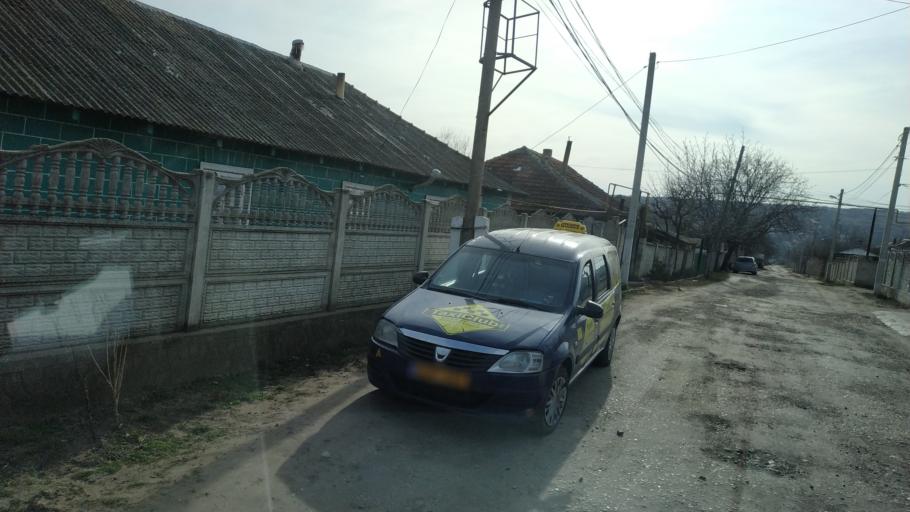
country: MD
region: Chisinau
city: Vatra
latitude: 47.0773
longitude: 28.6871
